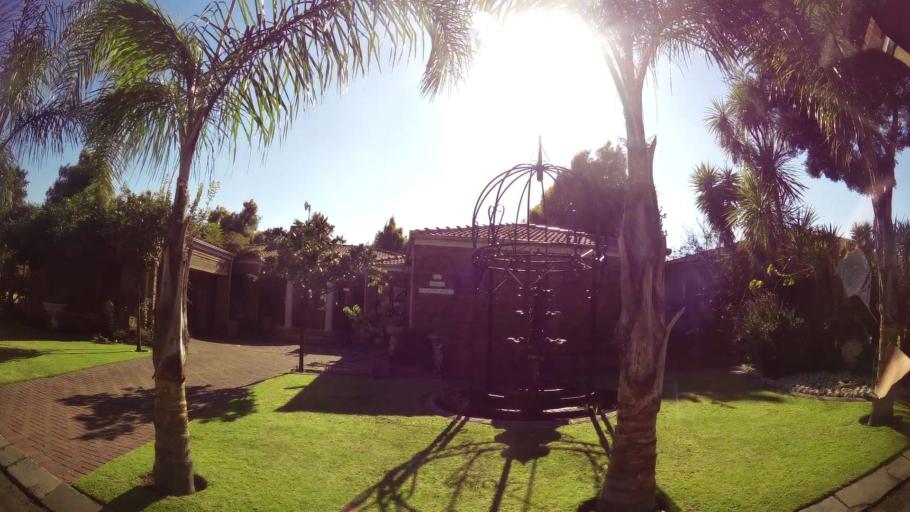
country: ZA
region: Mpumalanga
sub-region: Nkangala District Municipality
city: Witbank
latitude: -25.8914
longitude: 29.2479
